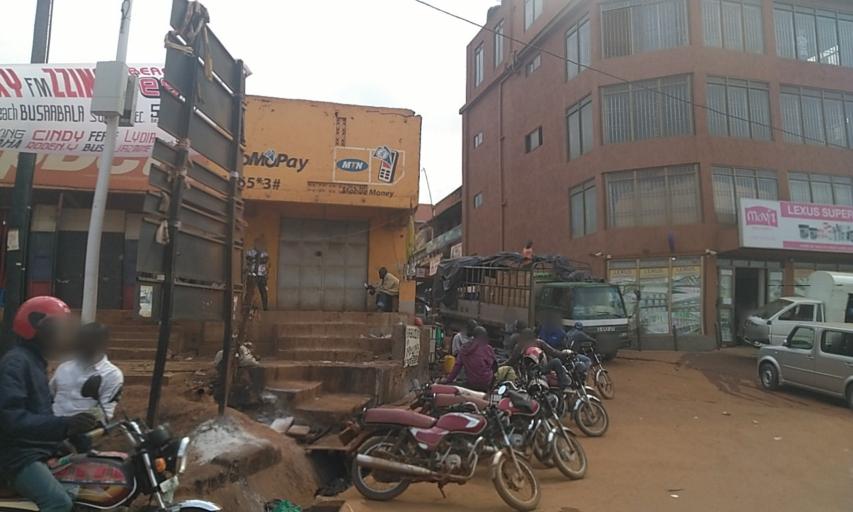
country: UG
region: Central Region
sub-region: Kampala District
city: Kampala
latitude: 0.2685
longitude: 32.5662
